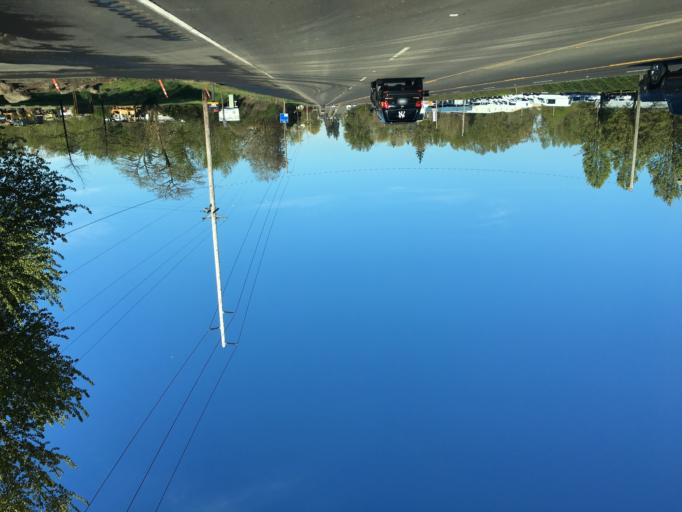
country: US
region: Oregon
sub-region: Clackamas County
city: Canby
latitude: 45.2539
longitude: -122.7136
